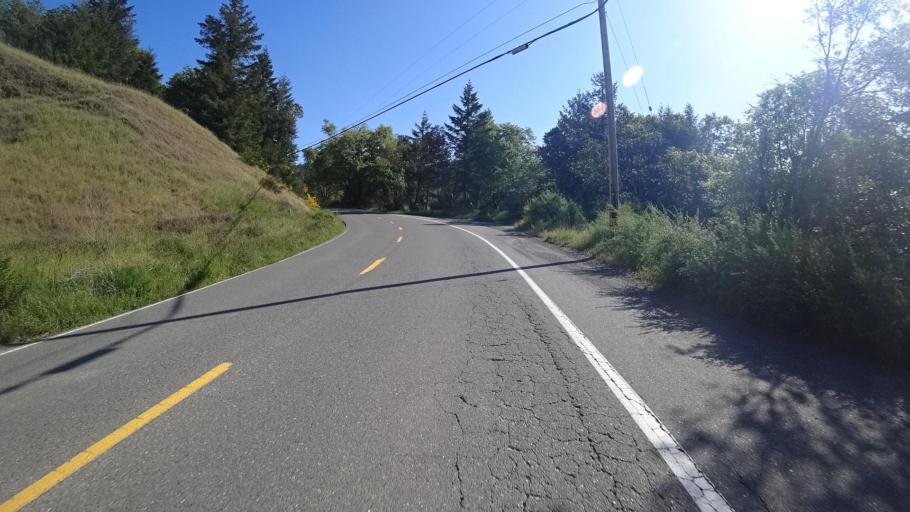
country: US
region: California
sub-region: Humboldt County
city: Redway
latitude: 40.1057
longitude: -123.7860
